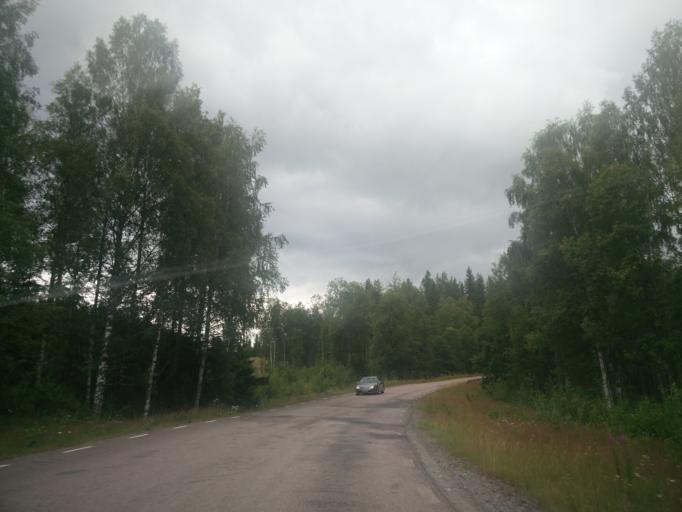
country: SE
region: Vaermland
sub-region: Arvika Kommun
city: Arvika
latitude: 59.9171
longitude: 12.6548
